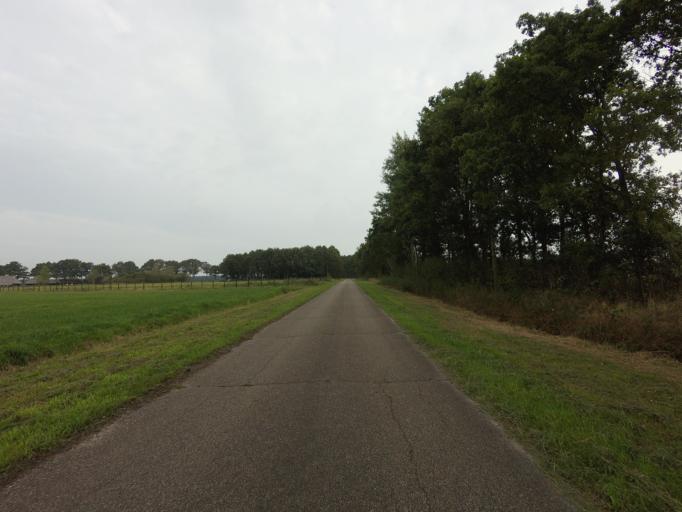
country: NL
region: Drenthe
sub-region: Gemeente Westerveld
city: Dwingeloo
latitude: 52.8596
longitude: 6.4114
